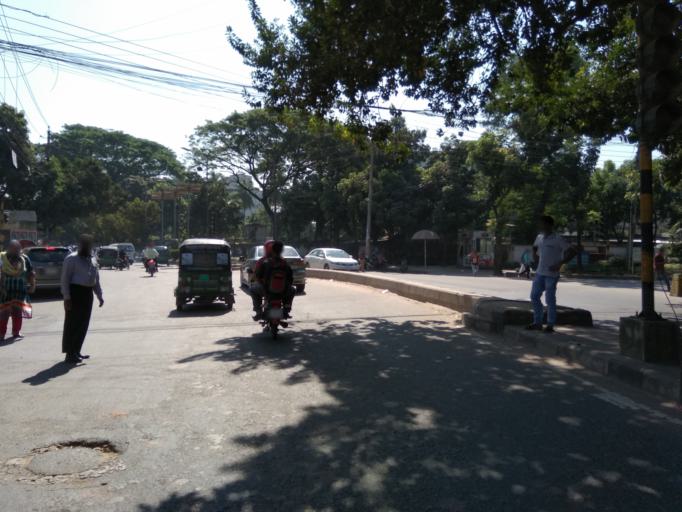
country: BD
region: Dhaka
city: Paltan
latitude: 23.7453
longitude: 90.4042
